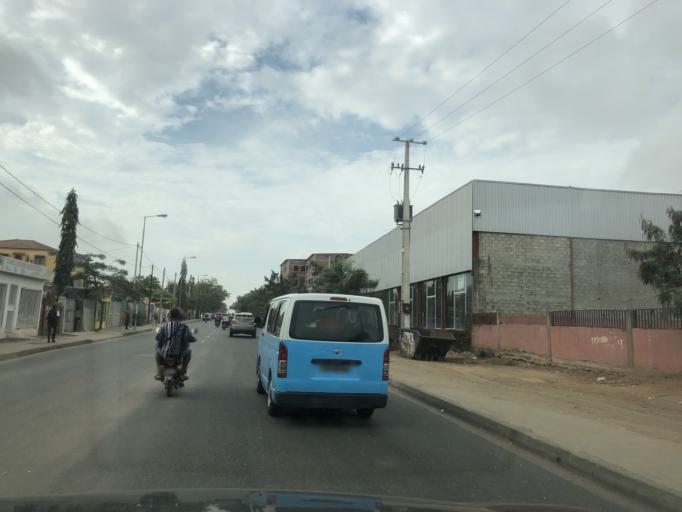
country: AO
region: Luanda
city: Luanda
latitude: -8.9169
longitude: 13.3727
